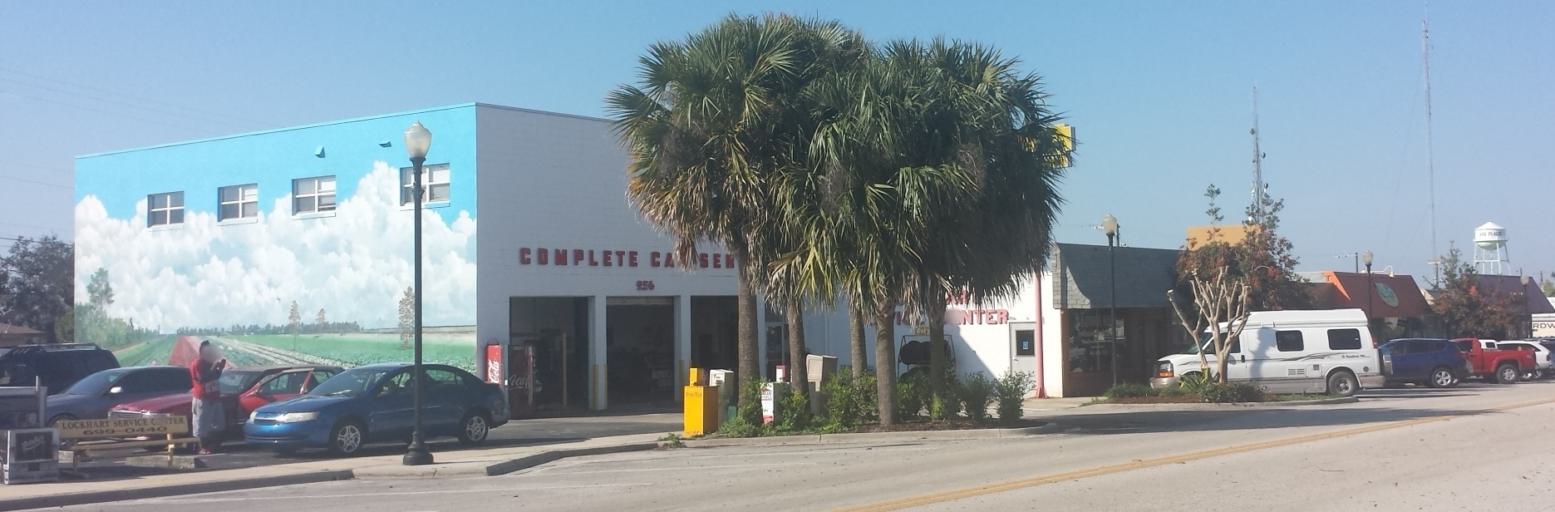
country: US
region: Florida
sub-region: Highlands County
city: Lake Placid
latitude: 27.2972
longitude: -81.3628
